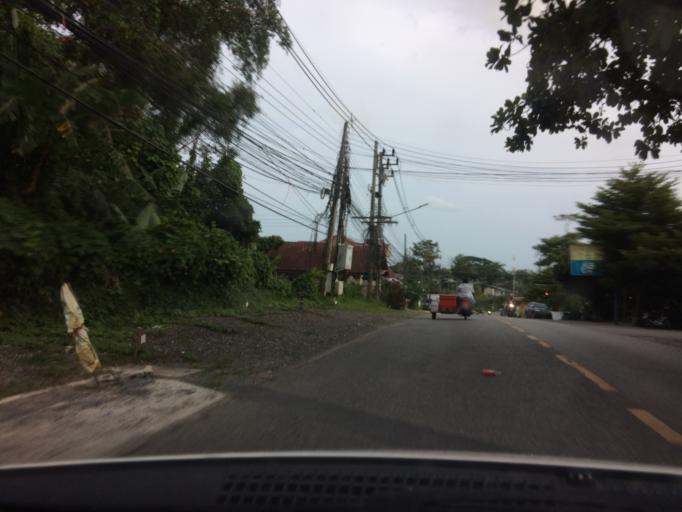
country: TH
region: Phuket
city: Phuket
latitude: 7.8927
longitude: 98.4072
